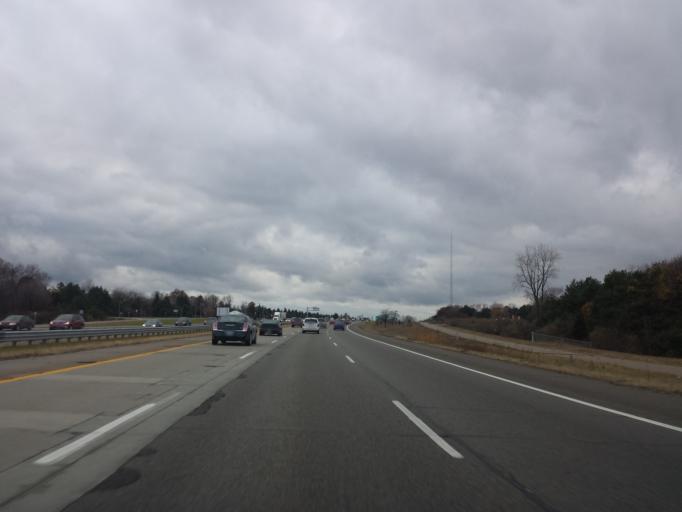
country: US
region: Michigan
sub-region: Oakland County
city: Pontiac
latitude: 42.7067
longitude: -83.3257
